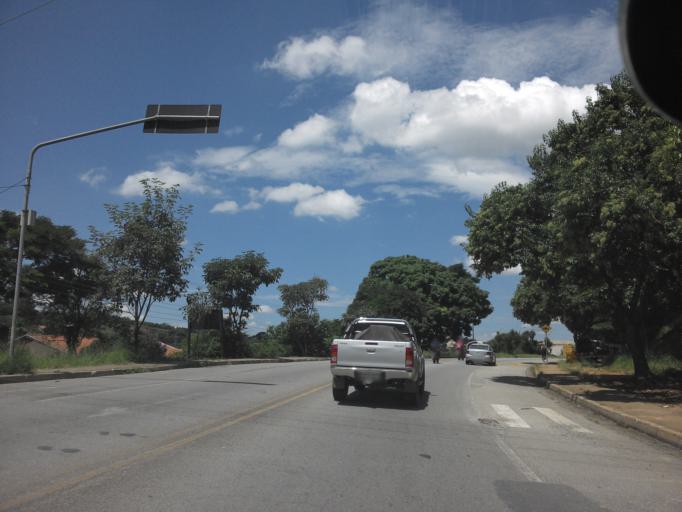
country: BR
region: Sao Paulo
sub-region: Taubate
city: Taubate
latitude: -23.0466
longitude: -45.5555
